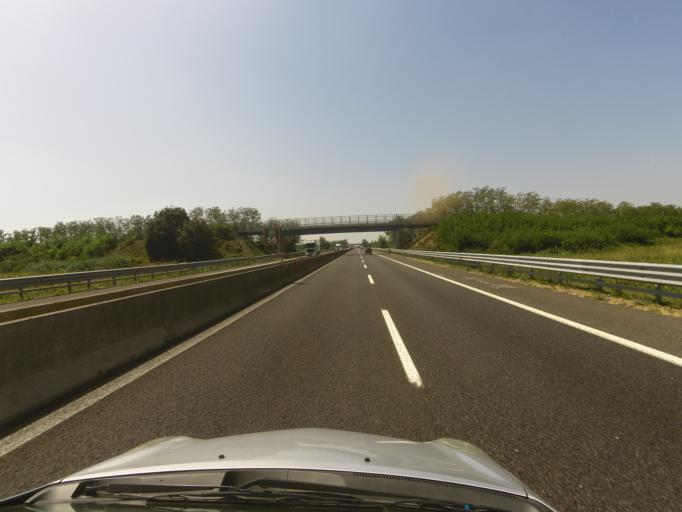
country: IT
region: Veneto
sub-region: Provincia di Rovigo
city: Frassinelle Polesine
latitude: 44.9915
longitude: 11.6677
